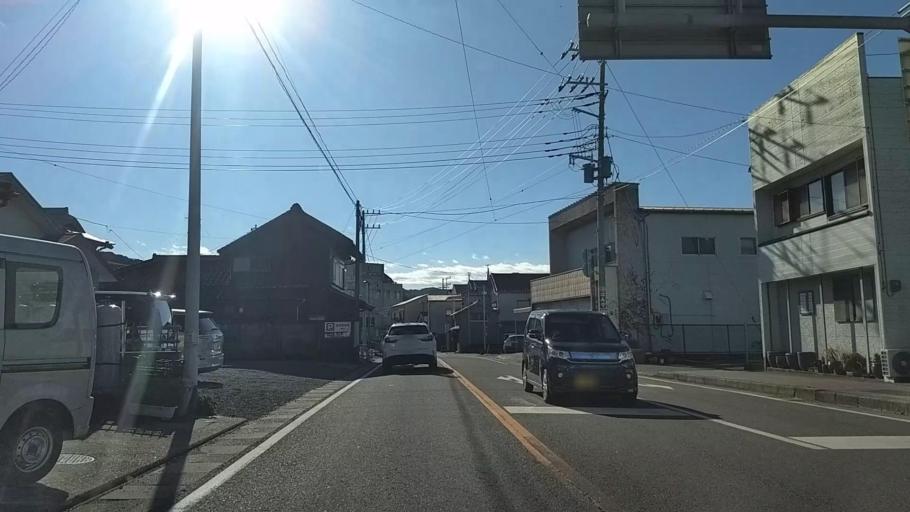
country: JP
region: Chiba
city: Tateyama
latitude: 35.1384
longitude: 139.8385
